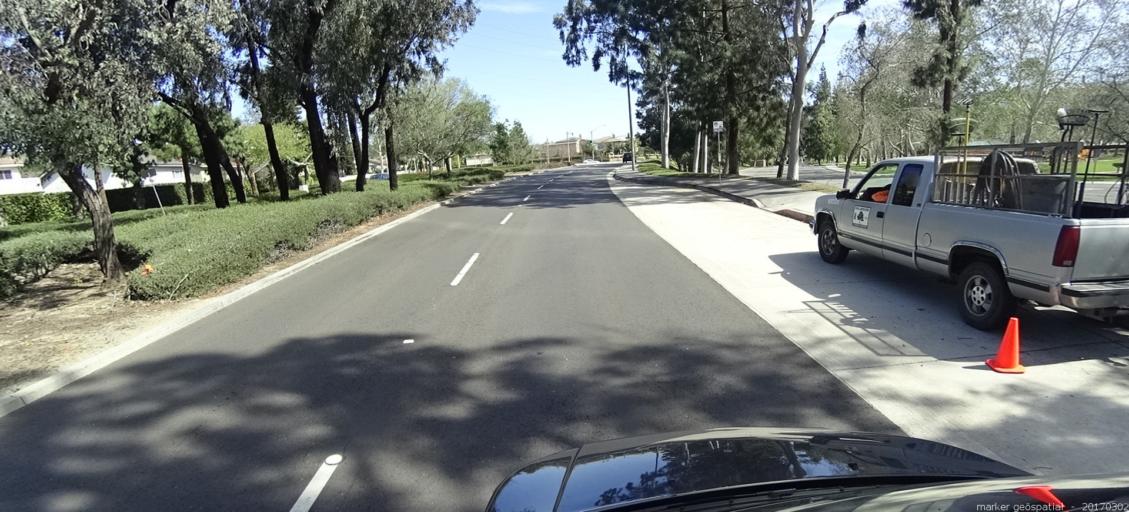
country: US
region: California
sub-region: Orange County
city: Yorba Linda
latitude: 33.8732
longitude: -117.7576
